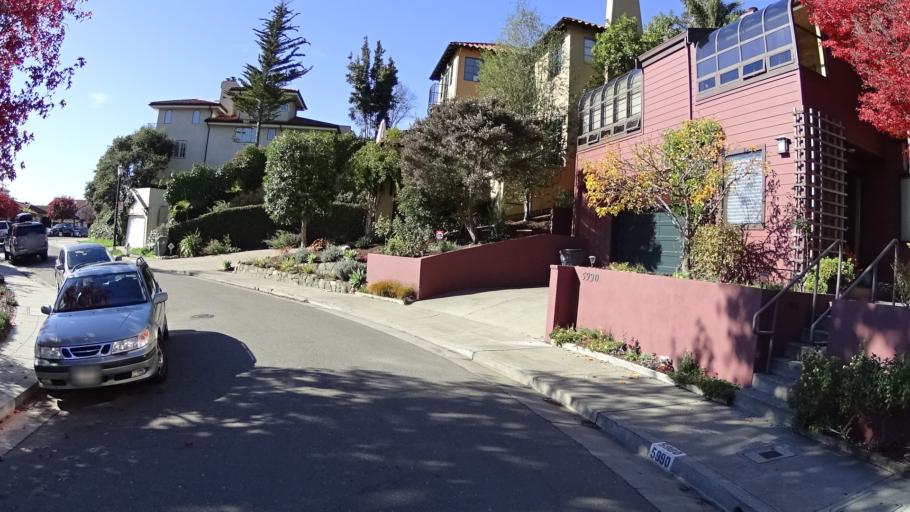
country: US
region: California
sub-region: Alameda County
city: Piedmont
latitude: 37.8462
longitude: -122.2340
